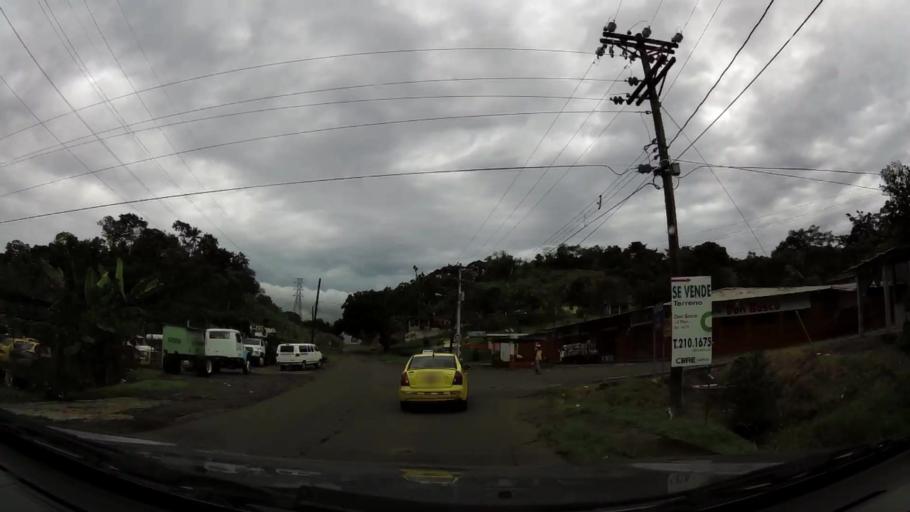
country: PA
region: Panama
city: Chilibre
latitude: 9.1355
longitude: -79.6132
